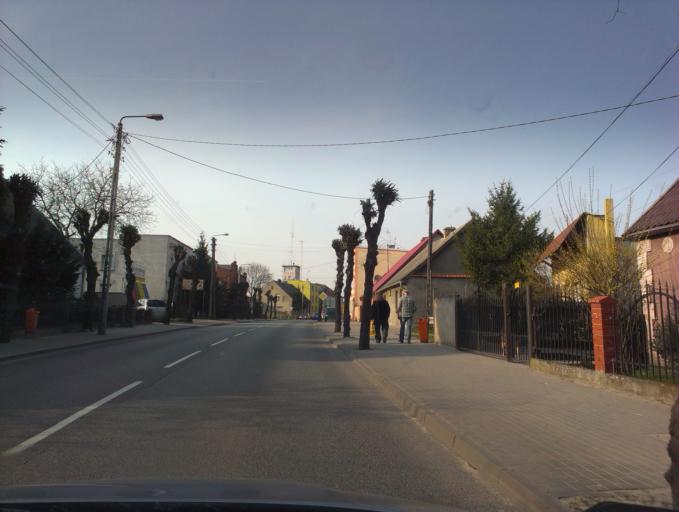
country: PL
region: Kujawsko-Pomorskie
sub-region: Powiat sepolenski
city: Sepolno Krajenskie
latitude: 53.4460
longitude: 17.5291
